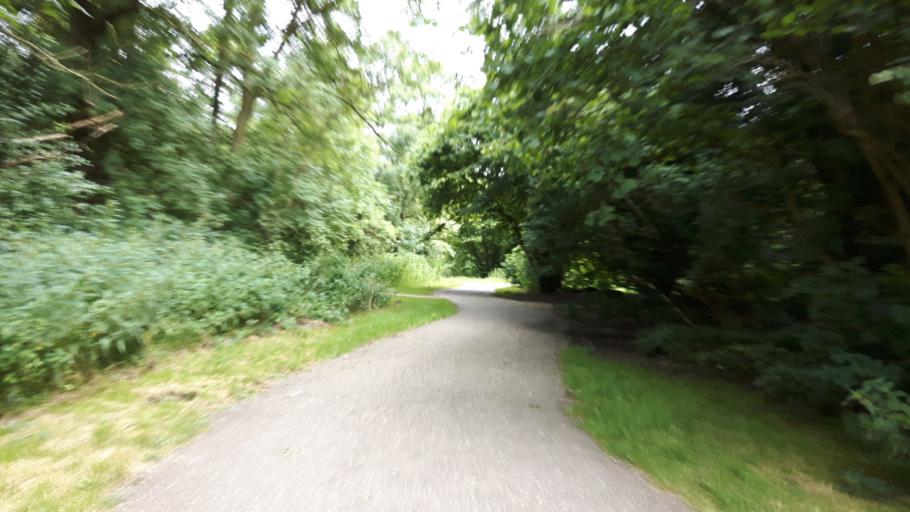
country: NL
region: South Holland
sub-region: Gemeente Lansingerland
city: Bergschenhoek
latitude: 51.9672
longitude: 4.5052
